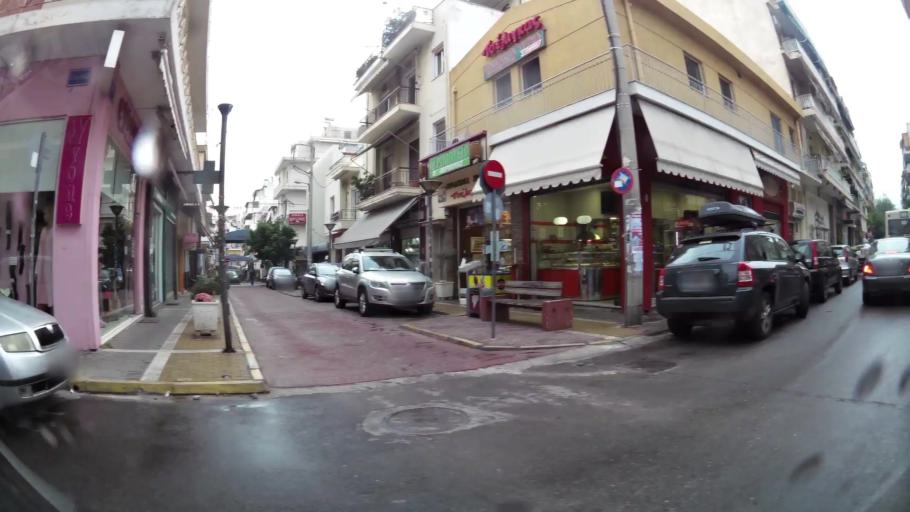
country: GR
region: Attica
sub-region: Nomarchia Athinas
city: Vyronas
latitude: 37.9583
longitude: 23.7529
